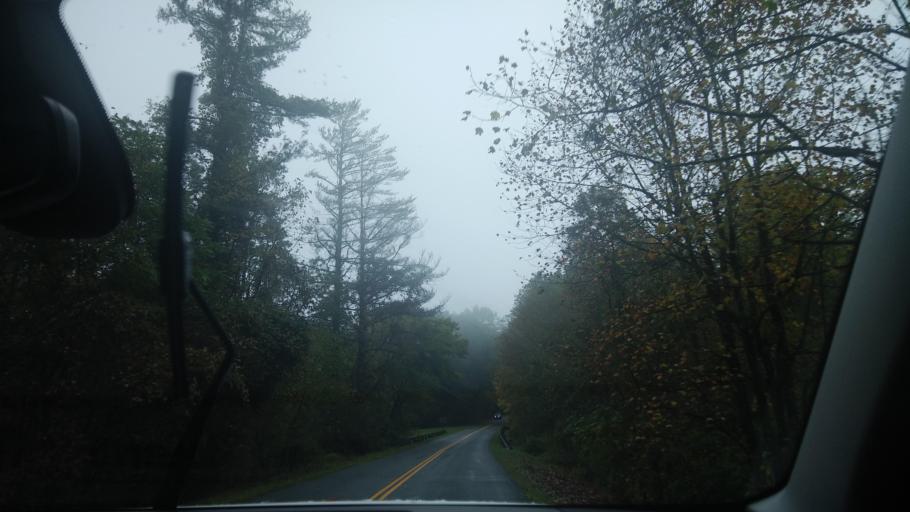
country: US
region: North Carolina
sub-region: Mitchell County
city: Spruce Pine
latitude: 35.8849
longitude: -82.0141
